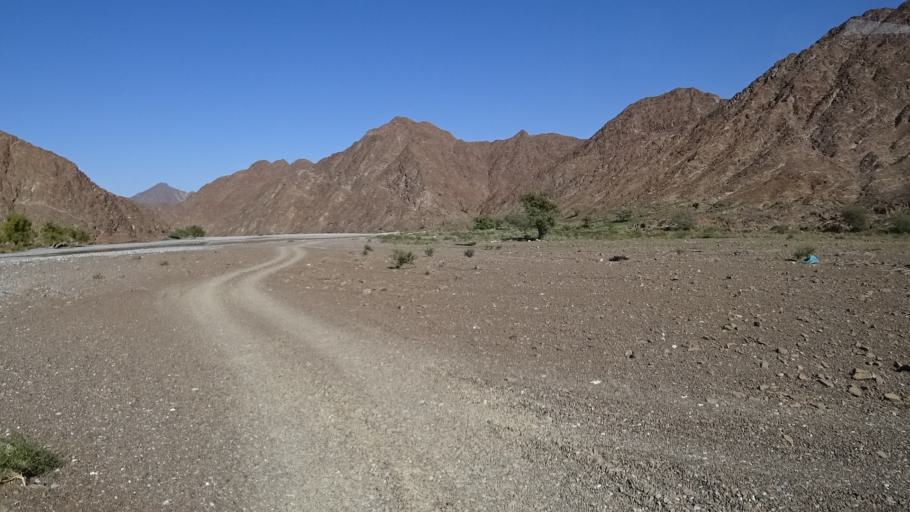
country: OM
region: Al Batinah
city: Bayt al `Awabi
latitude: 23.3991
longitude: 57.6643
